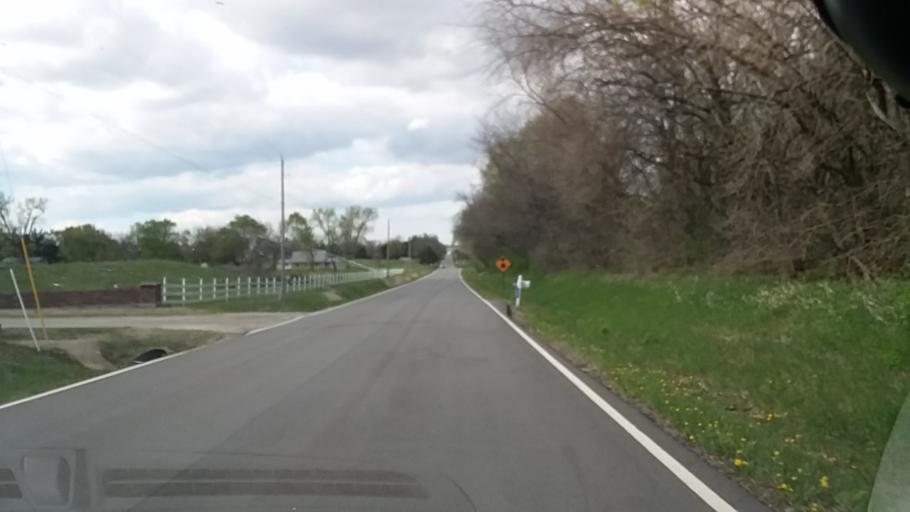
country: US
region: Kansas
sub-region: Douglas County
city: Lawrence
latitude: 38.8963
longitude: -95.2418
